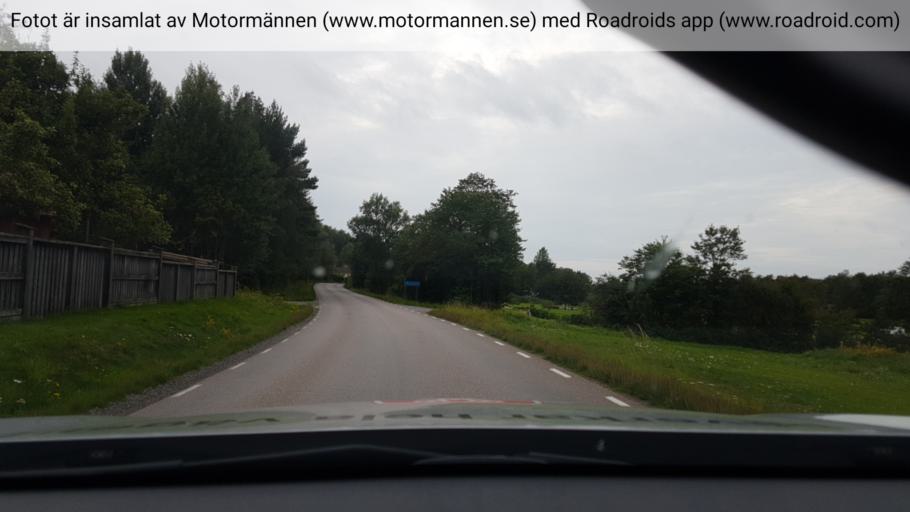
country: SE
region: Vaestra Goetaland
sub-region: Tanums Kommun
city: Grebbestad
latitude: 58.6360
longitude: 11.2900
